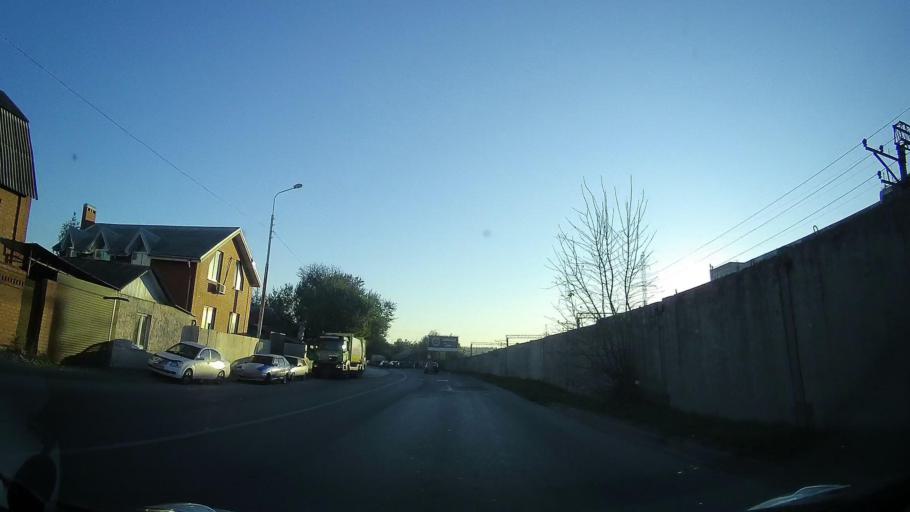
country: RU
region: Rostov
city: Rostov-na-Donu
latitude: 47.2441
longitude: 39.6745
